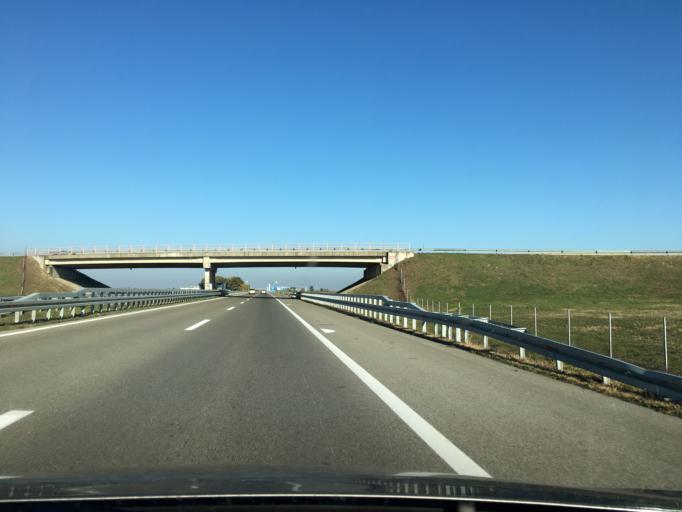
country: RS
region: Autonomna Pokrajina Vojvodina
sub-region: Severnobacki Okrug
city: Backa Topola
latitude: 45.7858
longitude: 19.6970
